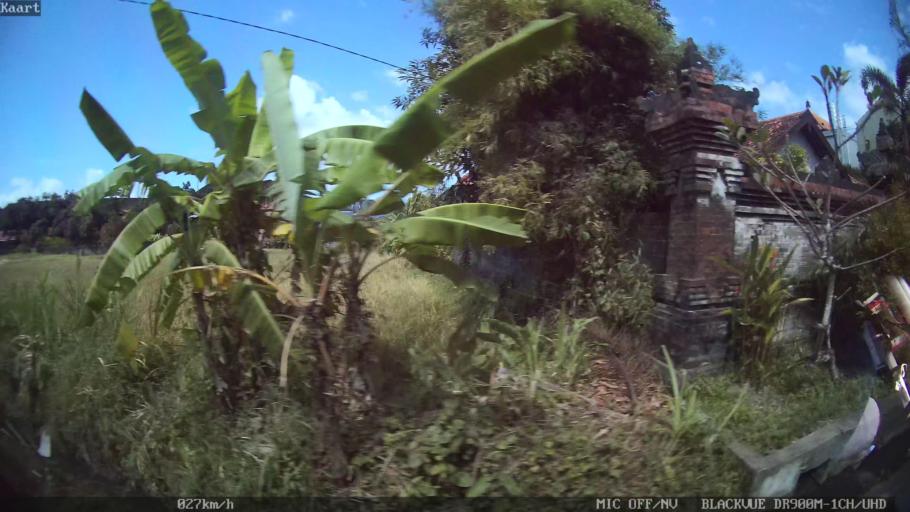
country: ID
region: Bali
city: Banjar Kertasari
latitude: -8.6283
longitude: 115.1782
